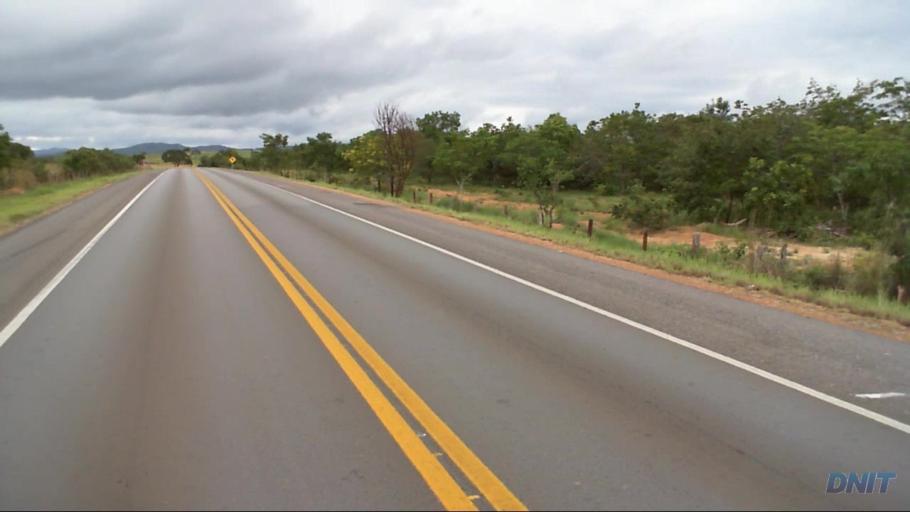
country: BR
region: Goias
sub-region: Padre Bernardo
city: Padre Bernardo
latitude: -15.2123
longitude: -48.5616
